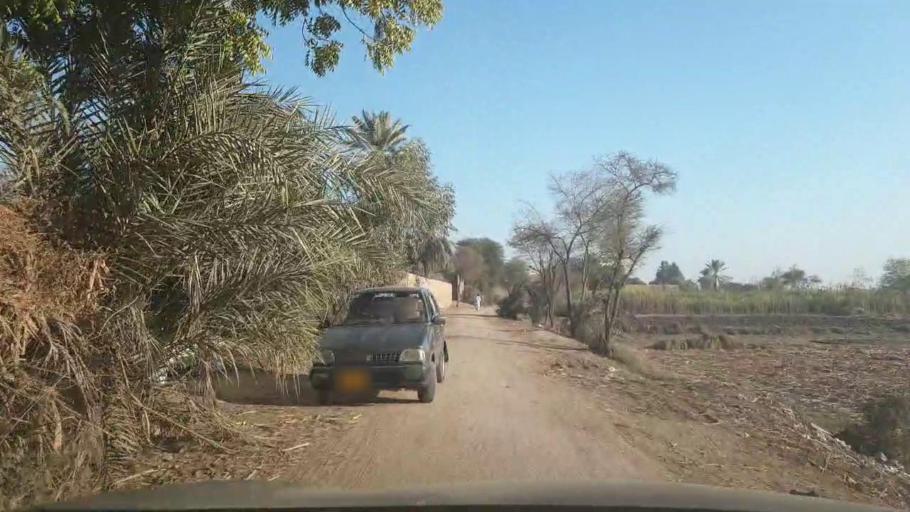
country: PK
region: Sindh
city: Ghotki
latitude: 28.0701
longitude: 69.3643
